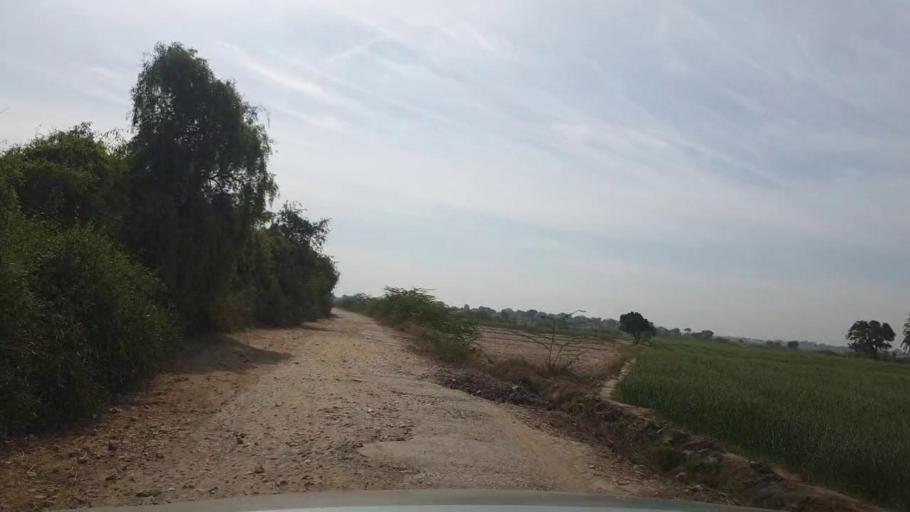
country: PK
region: Sindh
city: Kunri
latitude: 25.1596
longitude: 69.5974
